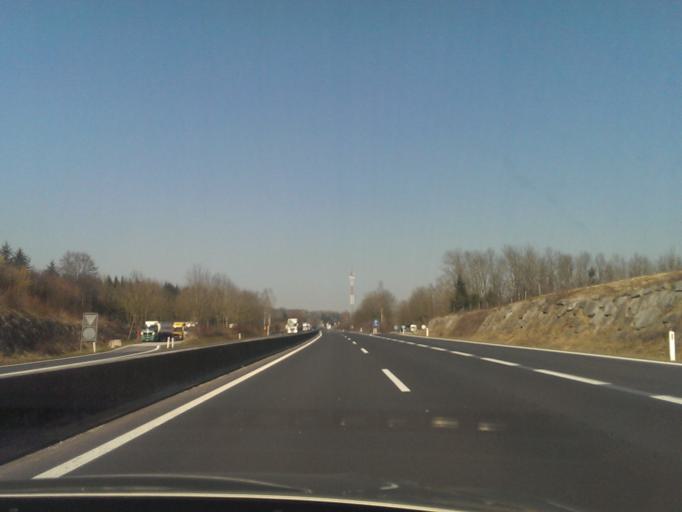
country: AT
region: Upper Austria
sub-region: Politischer Bezirk Kirchdorf an der Krems
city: Micheldorf in Oberoesterreich
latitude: 47.9571
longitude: 14.1005
